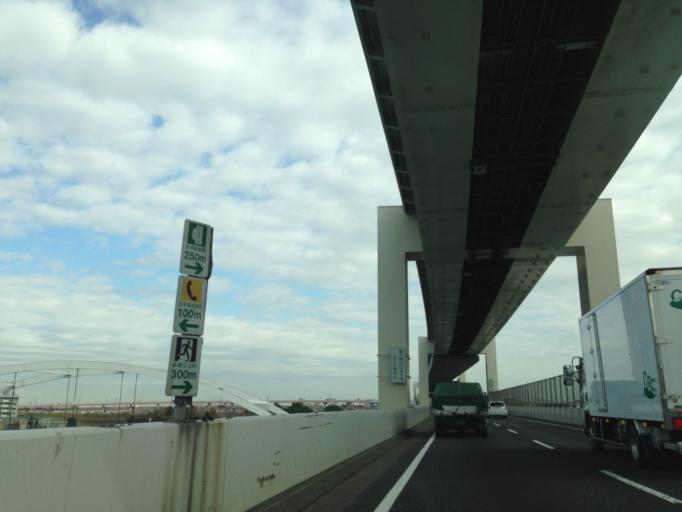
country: JP
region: Saitama
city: Kawaguchi
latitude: 35.7617
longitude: 139.7539
